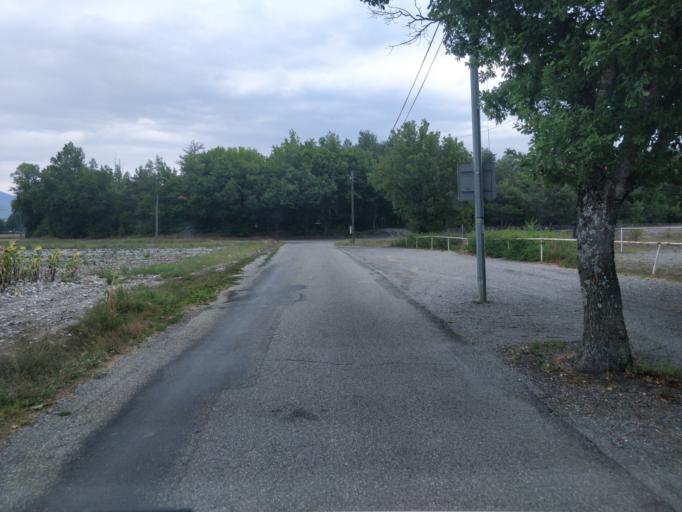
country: FR
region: Provence-Alpes-Cote d'Azur
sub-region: Departement des Alpes-de-Haute-Provence
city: Le Brusquet
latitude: 44.1343
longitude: 6.2702
